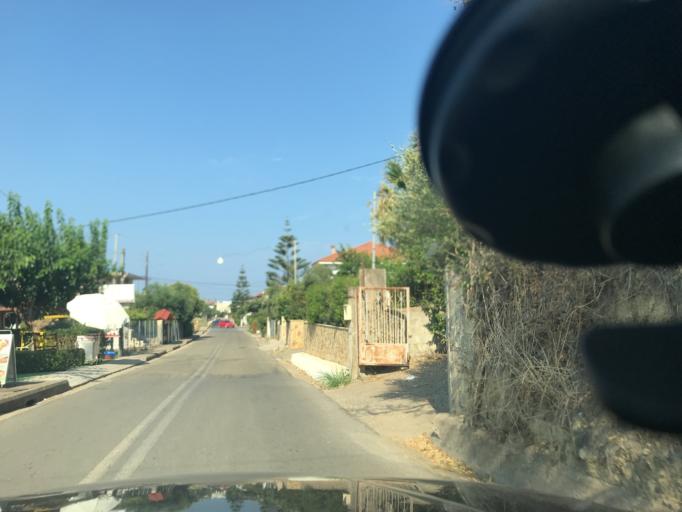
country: GR
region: West Greece
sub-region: Nomos Ileias
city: Kardamas
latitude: 37.7191
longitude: 21.3238
